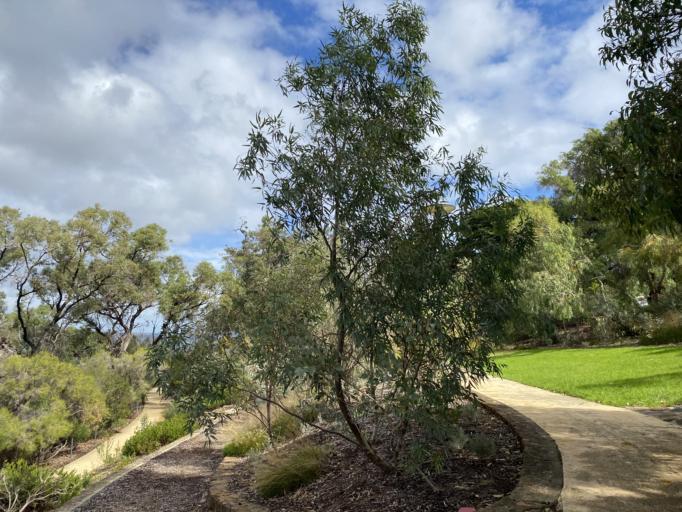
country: AU
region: Western Australia
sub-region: City of Perth
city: West Perth
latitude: -31.9616
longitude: 115.8422
